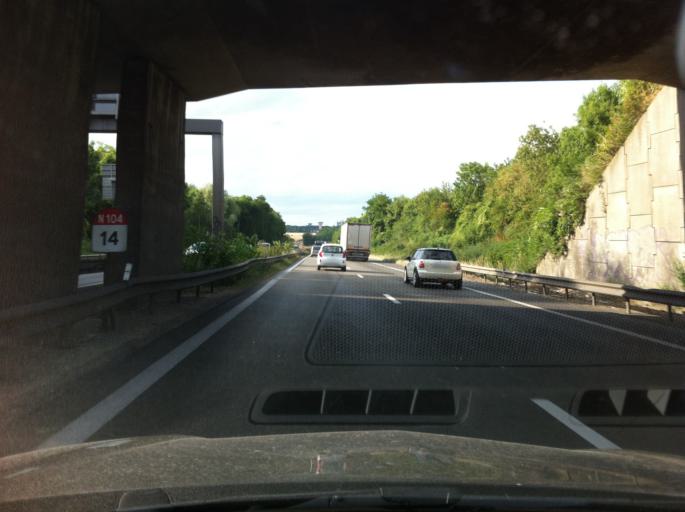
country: FR
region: Ile-de-France
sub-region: Departement de Seine-et-Marne
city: Servon
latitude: 48.7167
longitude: 2.5994
